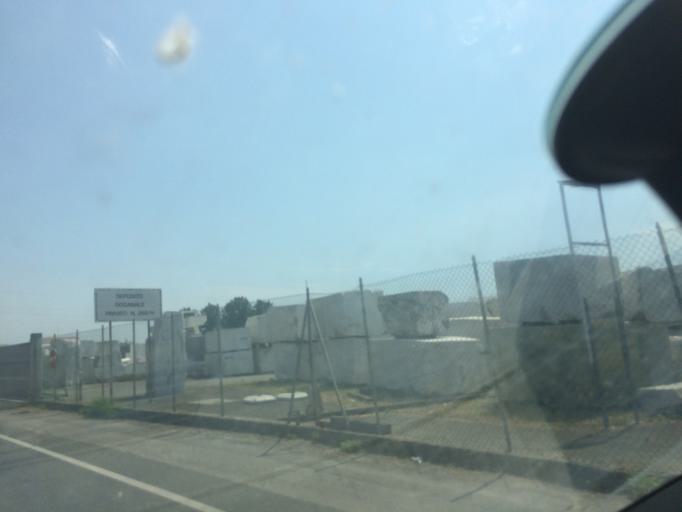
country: IT
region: Tuscany
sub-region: Provincia di Massa-Carrara
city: Carrara
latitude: 44.0341
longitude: 10.0839
